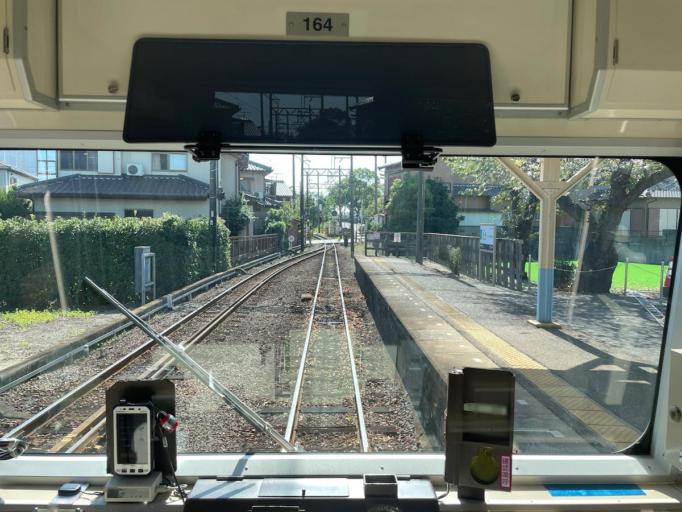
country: JP
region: Mie
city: Yokkaichi
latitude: 34.9557
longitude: 136.6041
